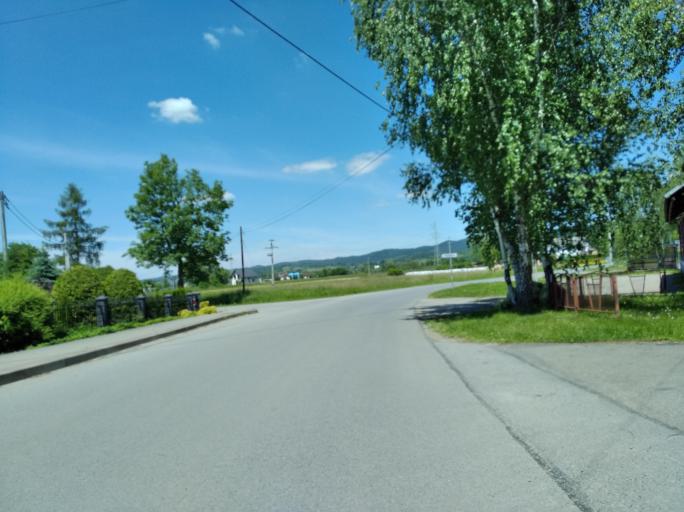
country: PL
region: Subcarpathian Voivodeship
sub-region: Powiat krosnienski
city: Wojaszowka
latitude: 49.7795
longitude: 21.6730
